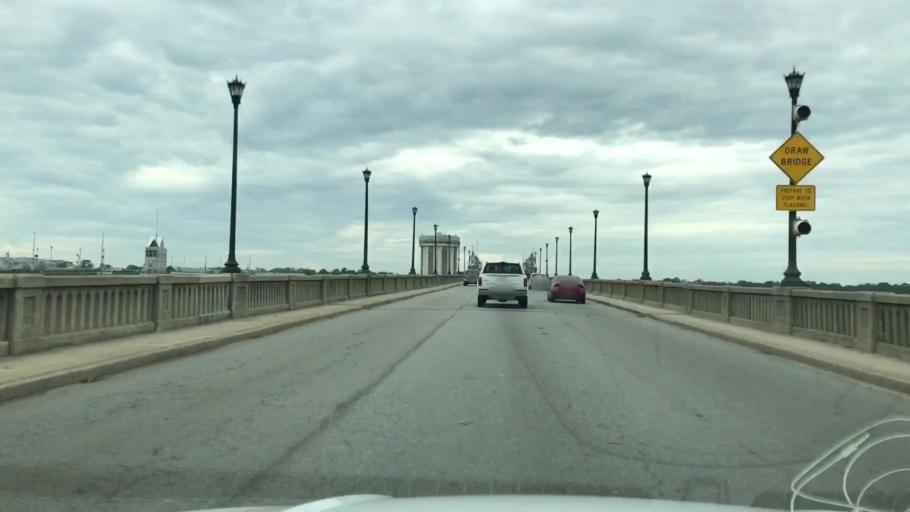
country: US
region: South Carolina
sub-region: Charleston County
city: Charleston
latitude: 32.7844
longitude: -79.9590
